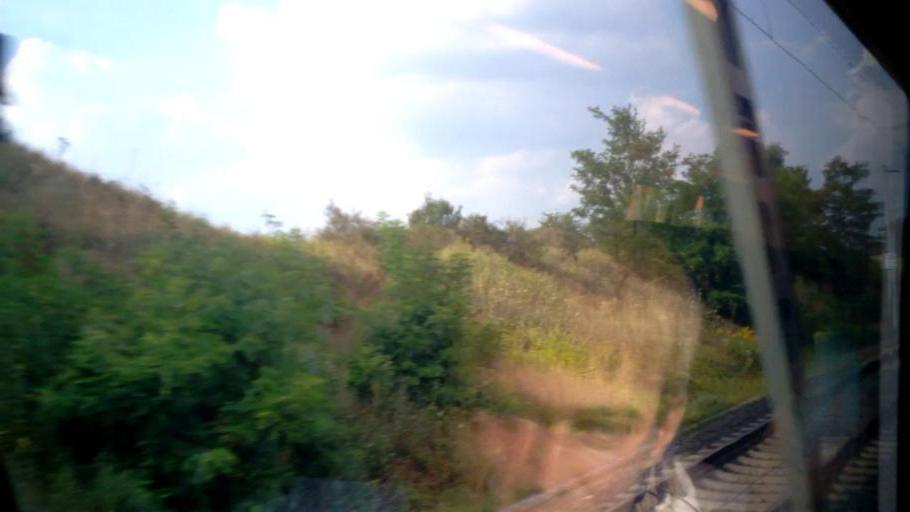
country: DE
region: Brandenburg
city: Grossbeeren
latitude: 52.3531
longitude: 13.2856
